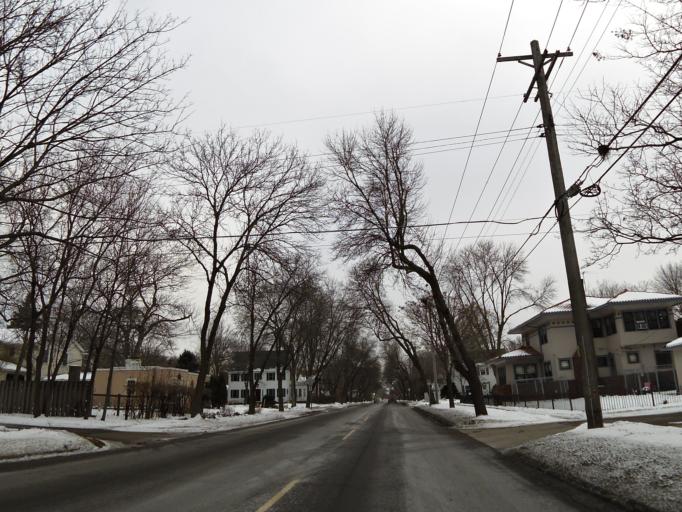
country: US
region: Minnesota
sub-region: Ramsey County
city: Falcon Heights
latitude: 44.9377
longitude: -93.1925
